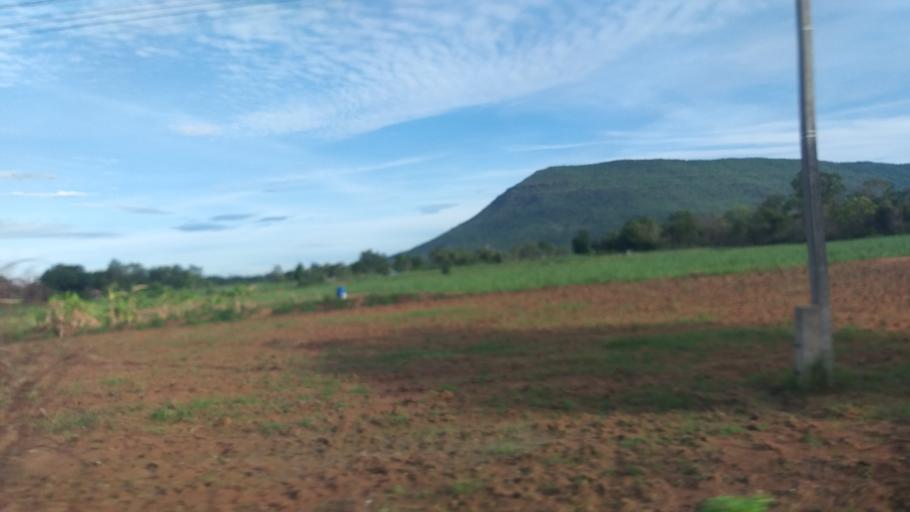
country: TH
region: Chaiyaphum
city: Ban Thaen
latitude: 16.3626
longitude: 102.2515
